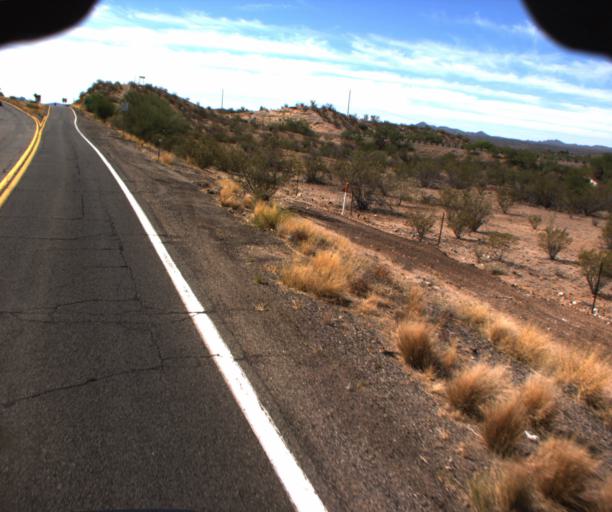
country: US
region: Arizona
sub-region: Maricopa County
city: Wickenburg
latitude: 34.0282
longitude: -112.8106
